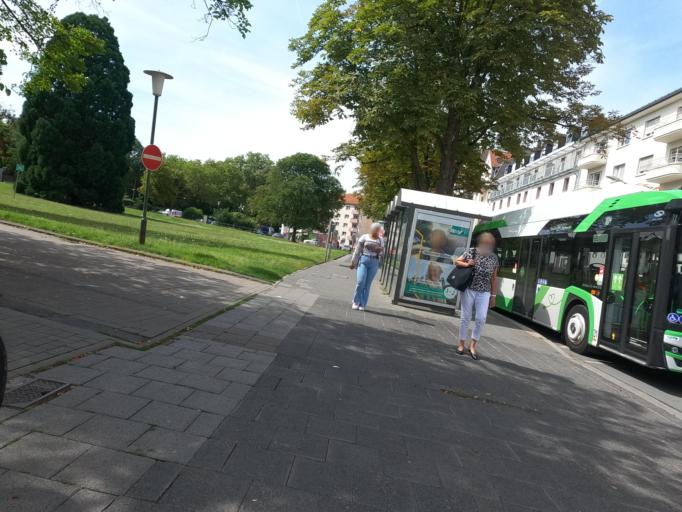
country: DE
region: Hesse
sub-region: Regierungsbezirk Darmstadt
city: Offenbach
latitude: 50.0961
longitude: 8.7564
